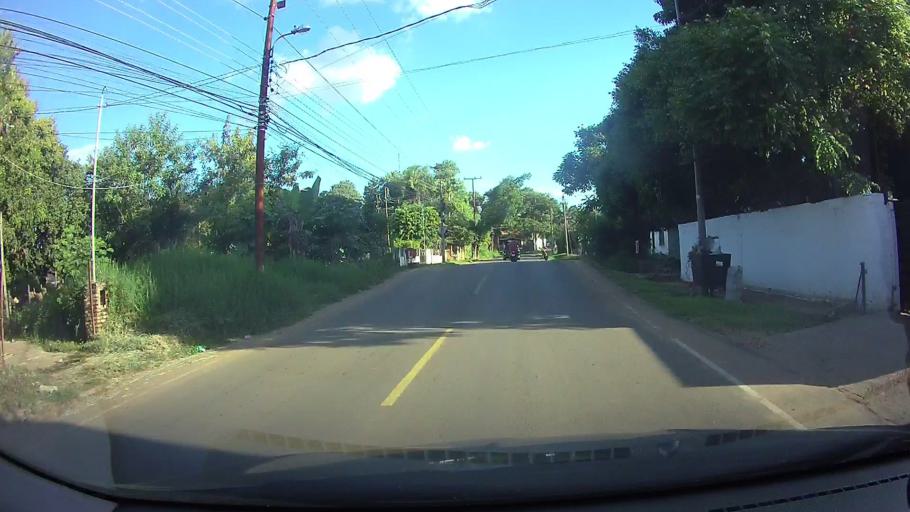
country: PY
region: Central
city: Fernando de la Mora
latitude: -25.2844
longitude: -57.5183
